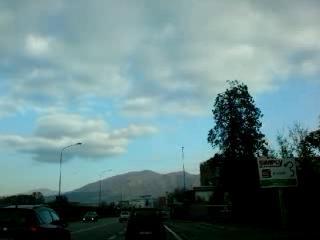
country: IT
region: Lombardy
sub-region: Provincia di Brescia
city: Collebeato
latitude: 45.5628
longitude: 10.2286
